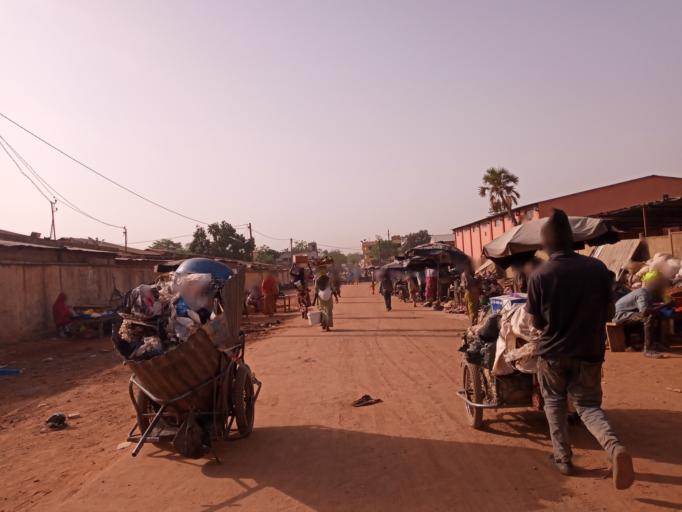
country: ML
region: Bamako
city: Bamako
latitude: 12.6574
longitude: -7.9897
